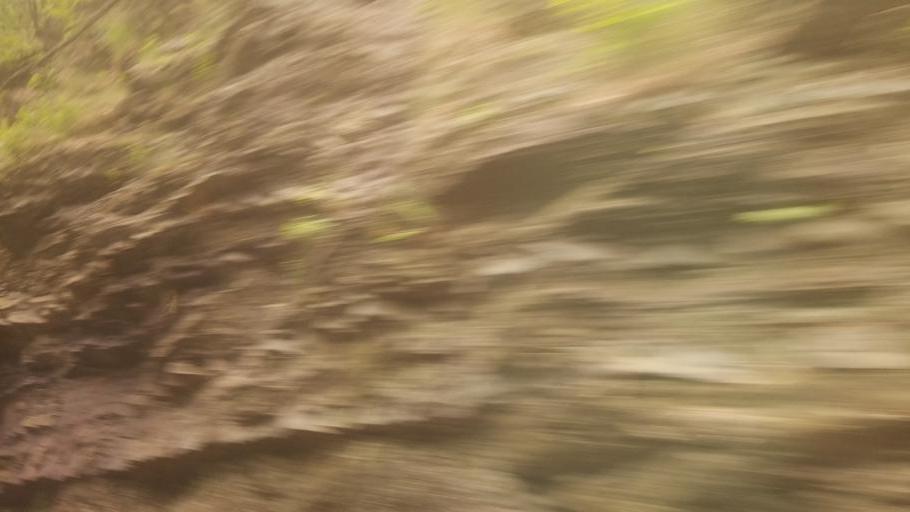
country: US
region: West Virginia
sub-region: Morgan County
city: Berkeley Springs
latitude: 39.5735
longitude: -78.4160
